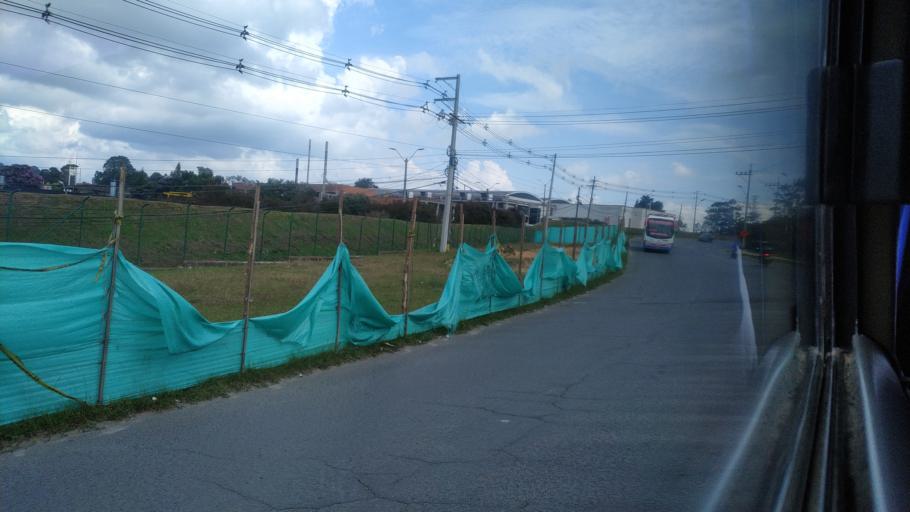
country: CO
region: Antioquia
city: Rionegro
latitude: 6.1671
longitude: -75.3679
